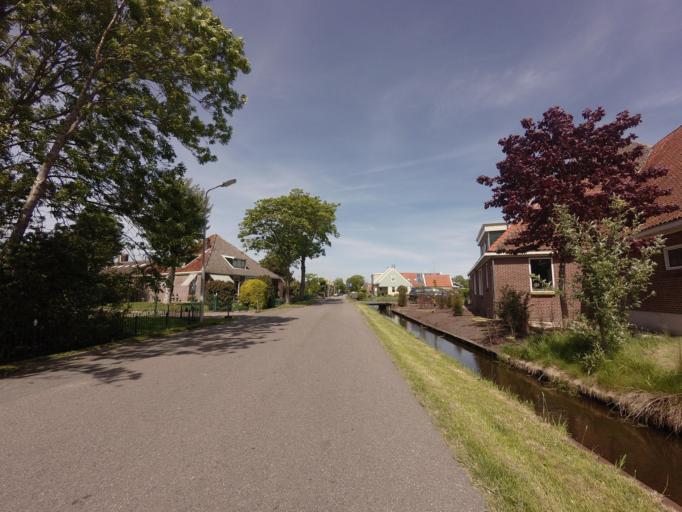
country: NL
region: North Holland
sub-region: Gemeente Velsen
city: Velsen-Zuid
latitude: 52.4466
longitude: 4.7215
